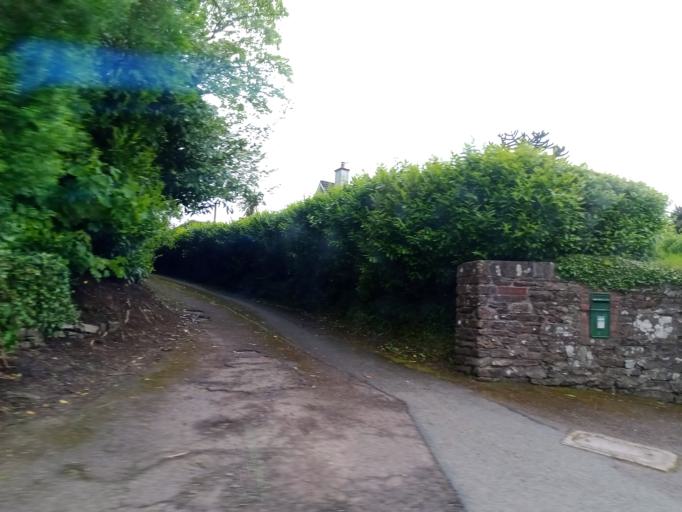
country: IE
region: Munster
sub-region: County Cork
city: Bandon
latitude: 51.7433
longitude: -8.7483
